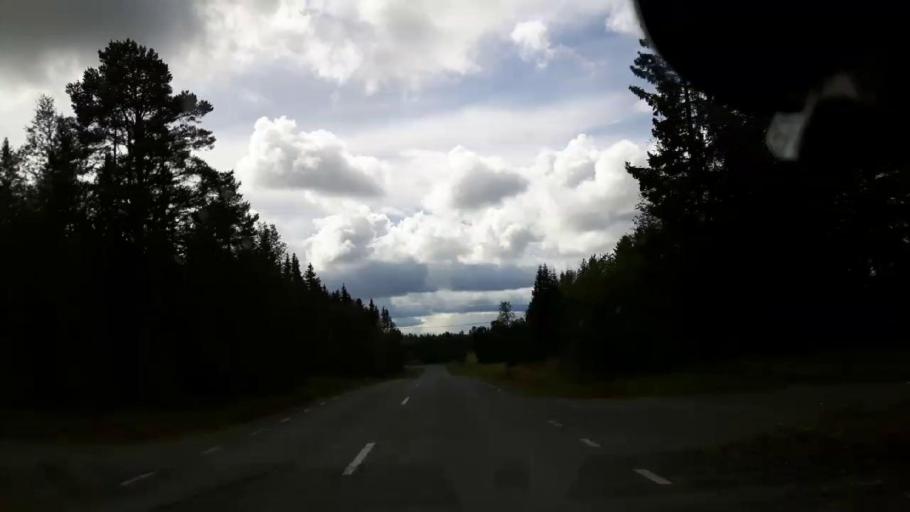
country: SE
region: Jaemtland
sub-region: Krokoms Kommun
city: Valla
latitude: 63.4329
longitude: 13.8109
